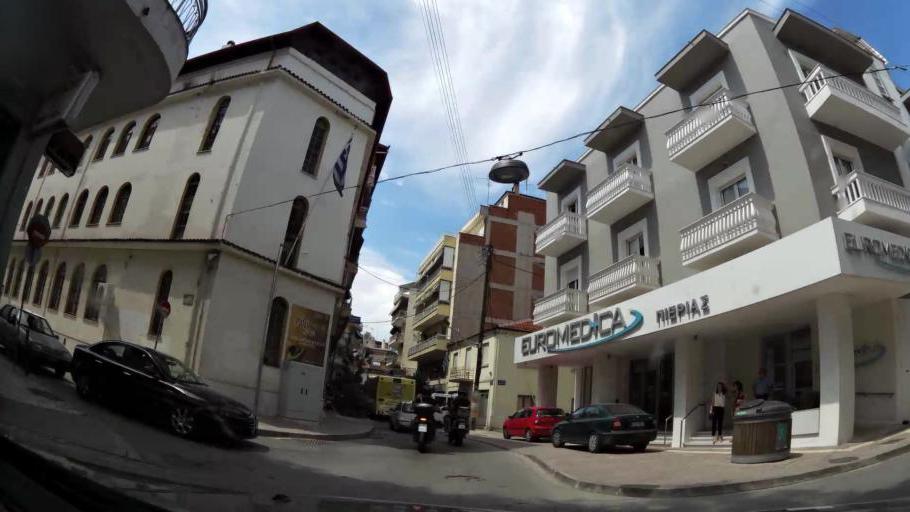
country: GR
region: Central Macedonia
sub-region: Nomos Pierias
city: Katerini
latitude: 40.2731
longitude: 22.5054
